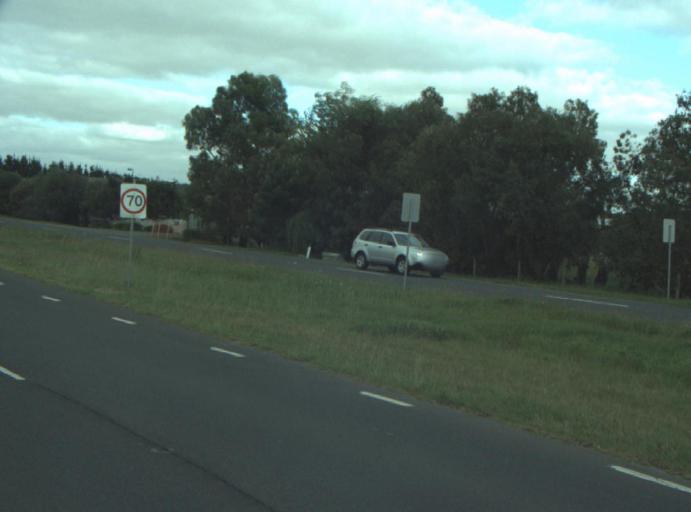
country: AU
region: Victoria
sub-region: Greater Geelong
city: Wandana Heights
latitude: -38.1983
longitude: 144.3164
